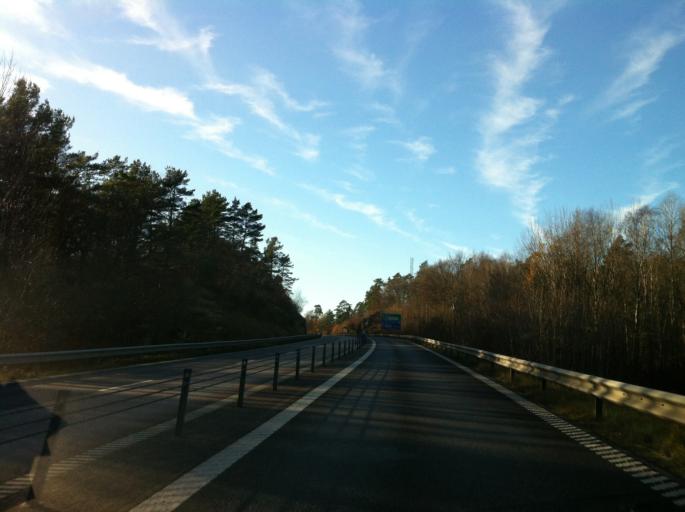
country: SE
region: Blekinge
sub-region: Karlshamns Kommun
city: Karlshamn
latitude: 56.1923
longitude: 14.8821
